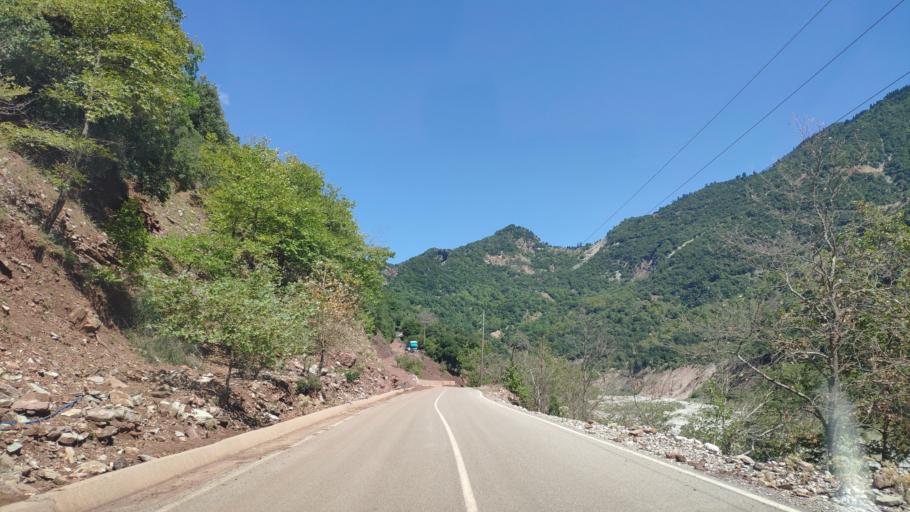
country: GR
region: Central Greece
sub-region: Nomos Evrytanias
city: Kerasochori
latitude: 39.0617
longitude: 21.6068
